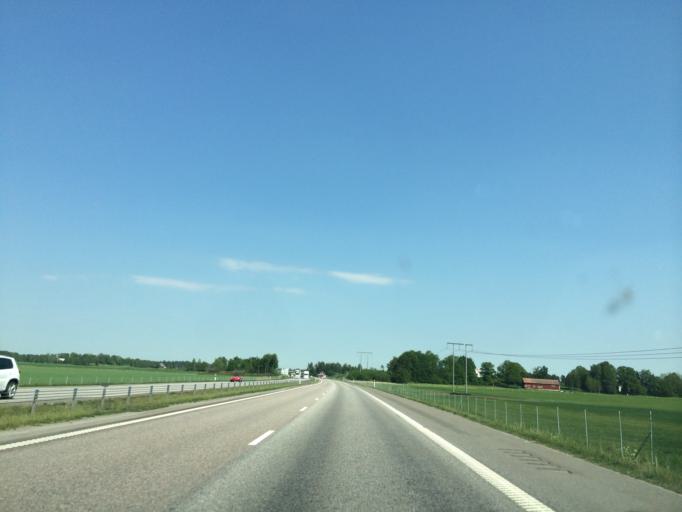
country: SE
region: OEstergoetland
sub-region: Linkopings Kommun
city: Ekangen
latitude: 58.4373
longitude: 15.7003
